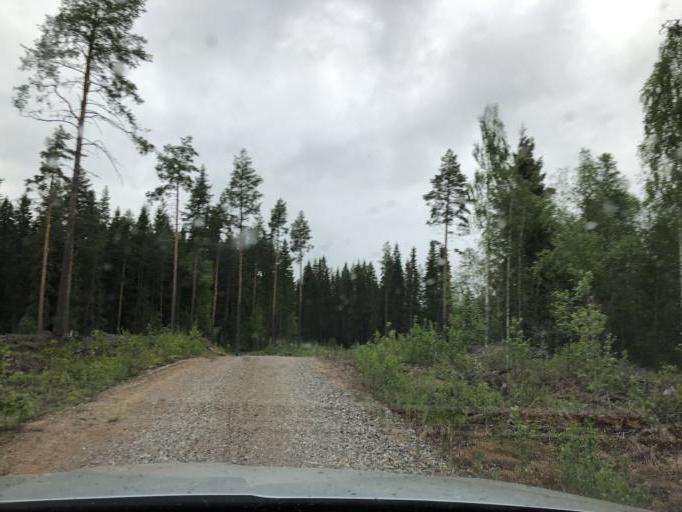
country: SE
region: Norrbotten
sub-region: Pitea Kommun
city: Roknas
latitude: 65.3991
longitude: 21.2690
